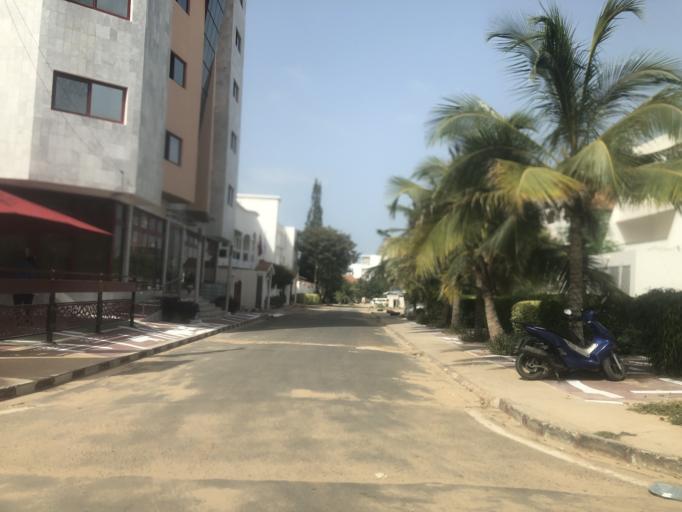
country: SN
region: Dakar
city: Mermoz Boabab
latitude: 14.7392
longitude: -17.5143
